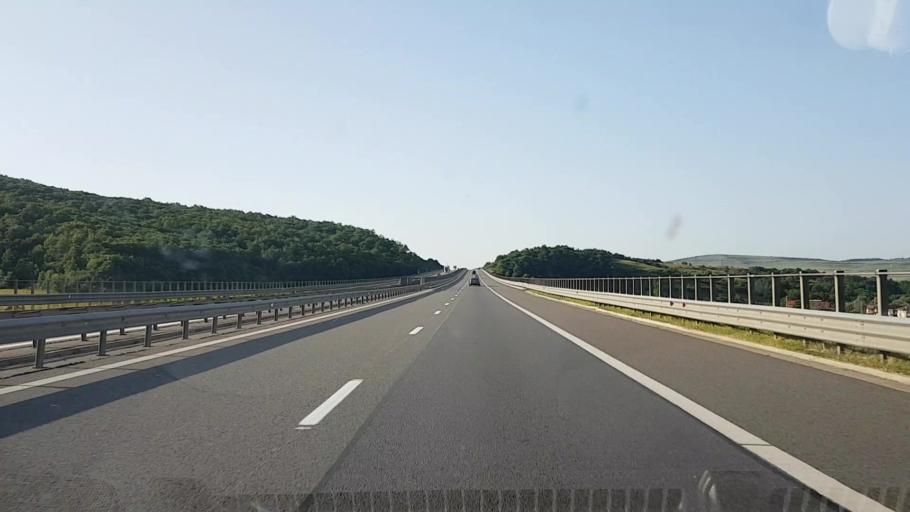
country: RO
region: Cluj
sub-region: Comuna Floresti
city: Luna de Sus
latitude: 46.7306
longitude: 23.4181
